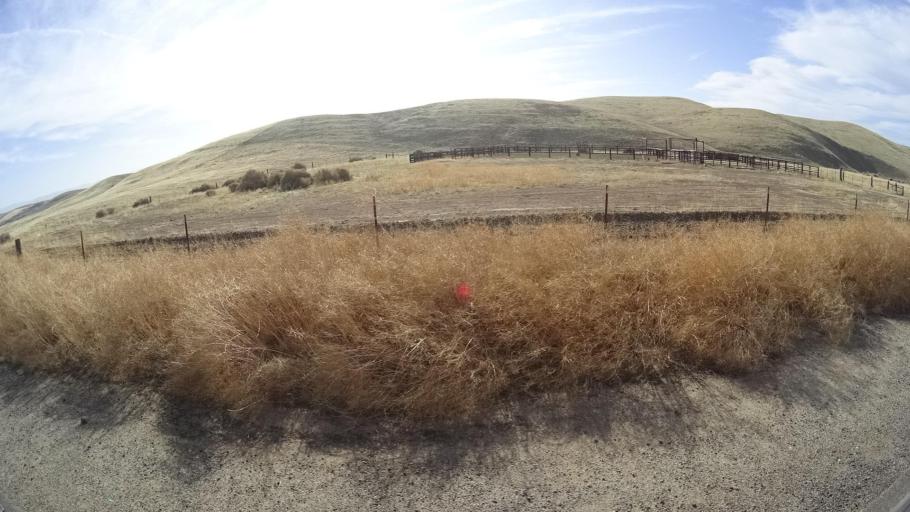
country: US
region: California
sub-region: Tulare County
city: Richgrove
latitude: 35.6263
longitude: -118.9967
